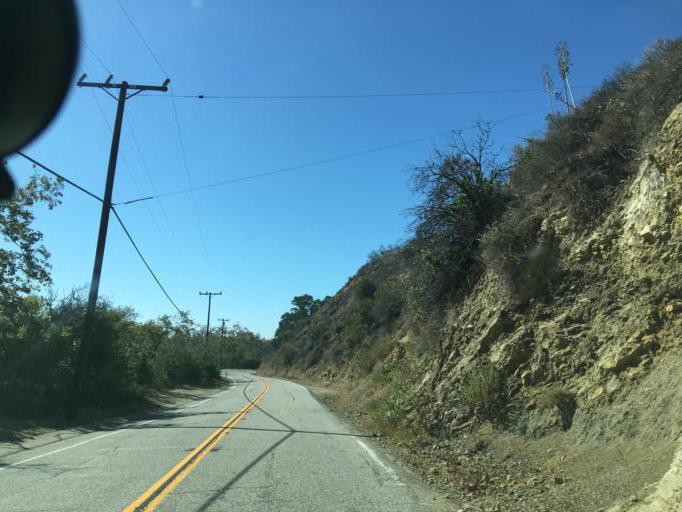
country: US
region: California
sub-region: Ventura County
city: Casa Conejo
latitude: 34.0506
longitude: -118.9357
